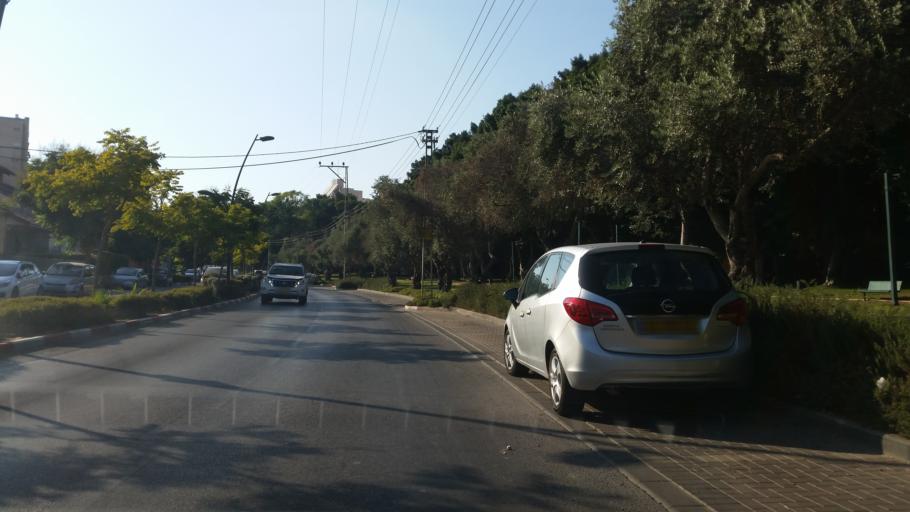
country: IL
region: Tel Aviv
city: Ramat HaSharon
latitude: 32.1300
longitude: 34.8552
